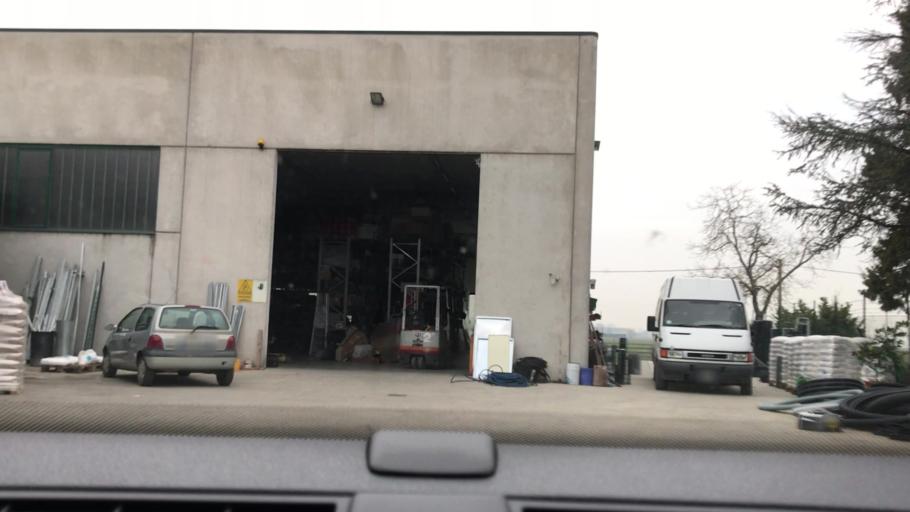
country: IT
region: Lombardy
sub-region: Provincia di Mantova
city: Dosolo
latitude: 44.9532
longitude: 10.6320
